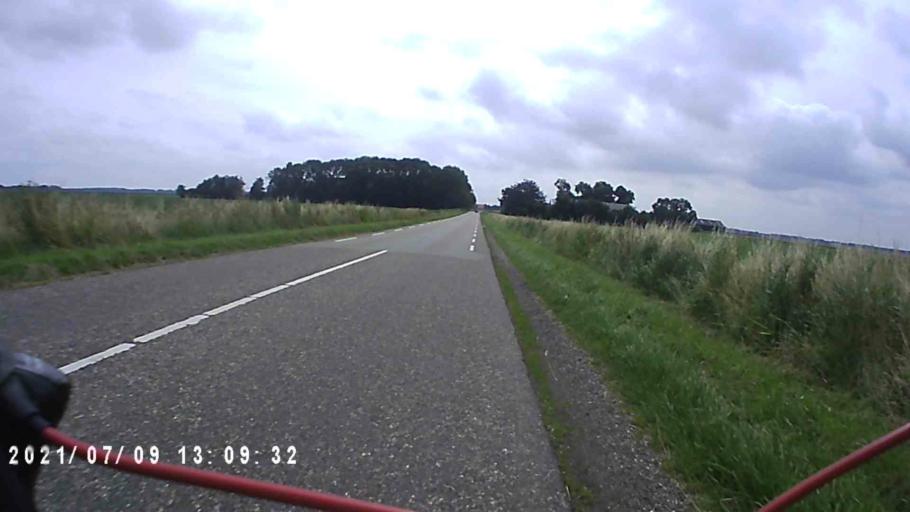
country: NL
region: Groningen
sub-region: Gemeente  Oldambt
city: Winschoten
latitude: 53.1294
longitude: 7.1181
